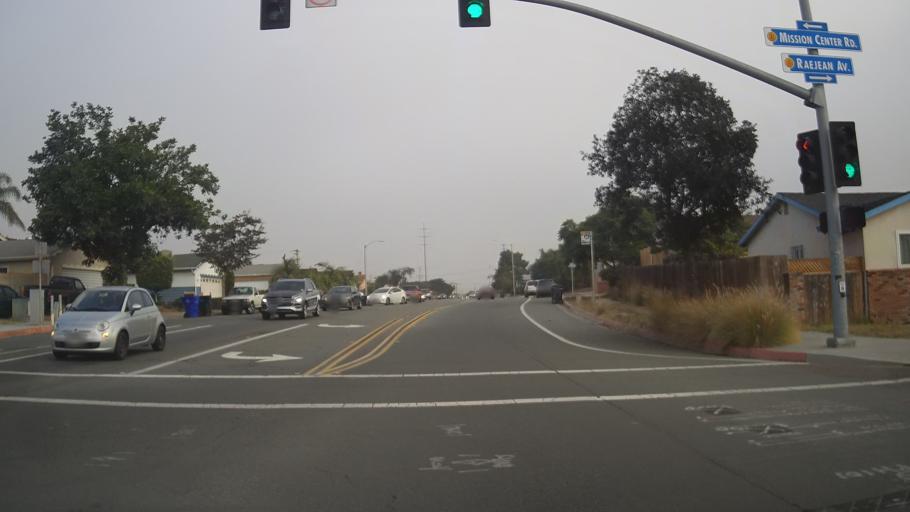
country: US
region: California
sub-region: San Diego County
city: San Diego
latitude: 32.7897
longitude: -117.1448
